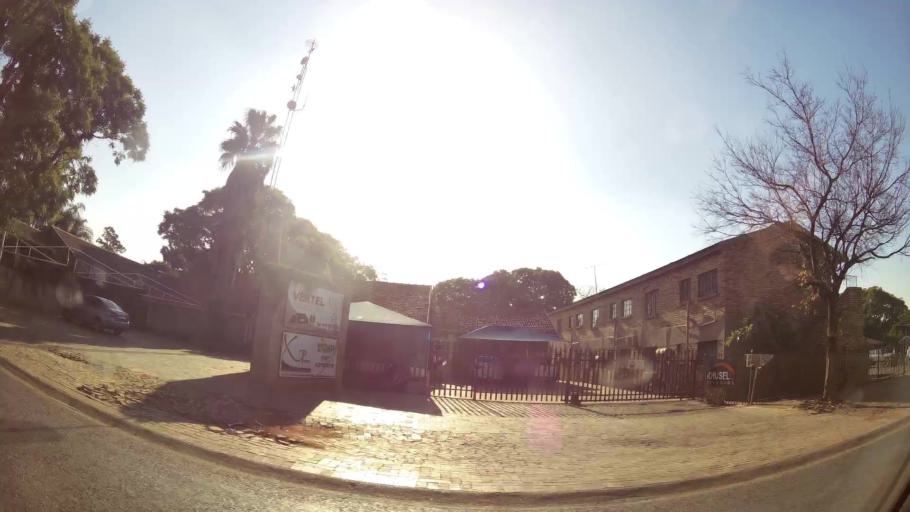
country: ZA
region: North-West
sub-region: Bojanala Platinum District Municipality
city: Rustenburg
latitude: -25.6729
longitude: 27.2515
